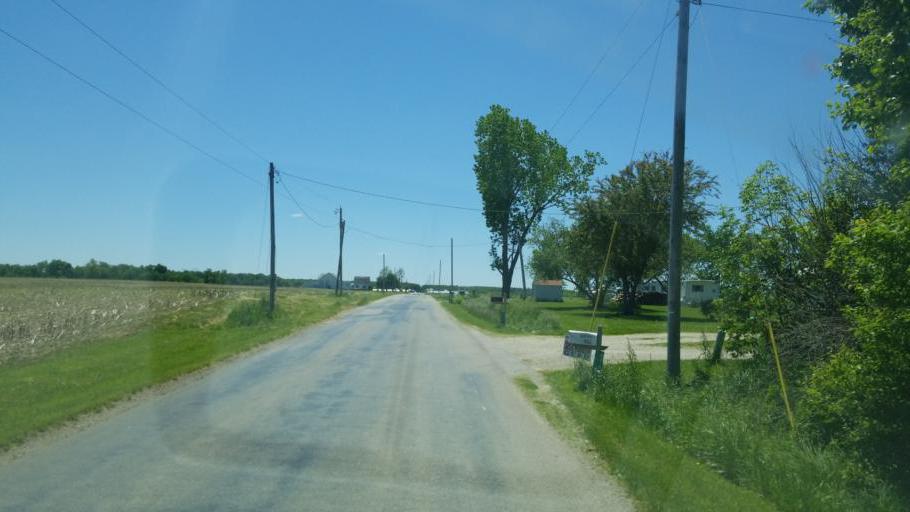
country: US
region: Ohio
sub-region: Mercer County
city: Fort Recovery
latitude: 40.3460
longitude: -84.8039
